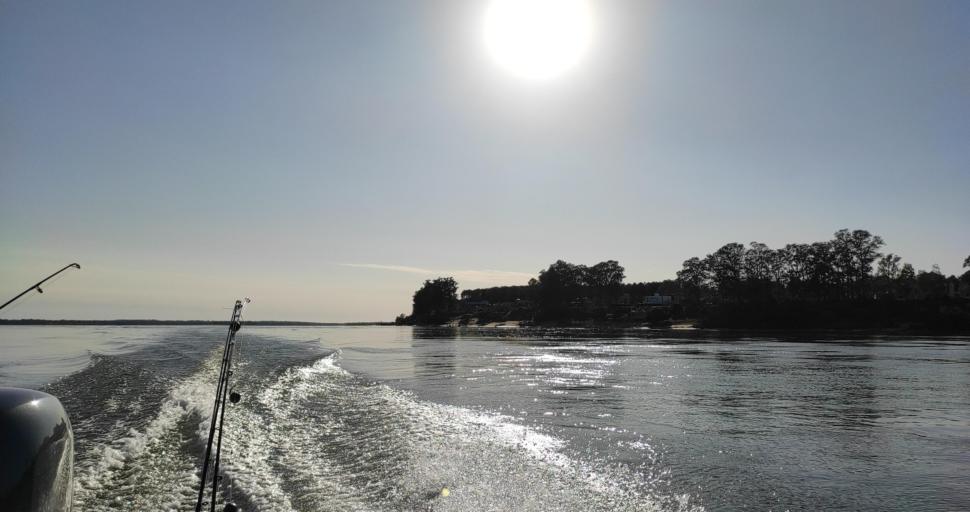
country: AR
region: Corrientes
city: Ituzaingo
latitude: -27.6005
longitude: -56.8189
